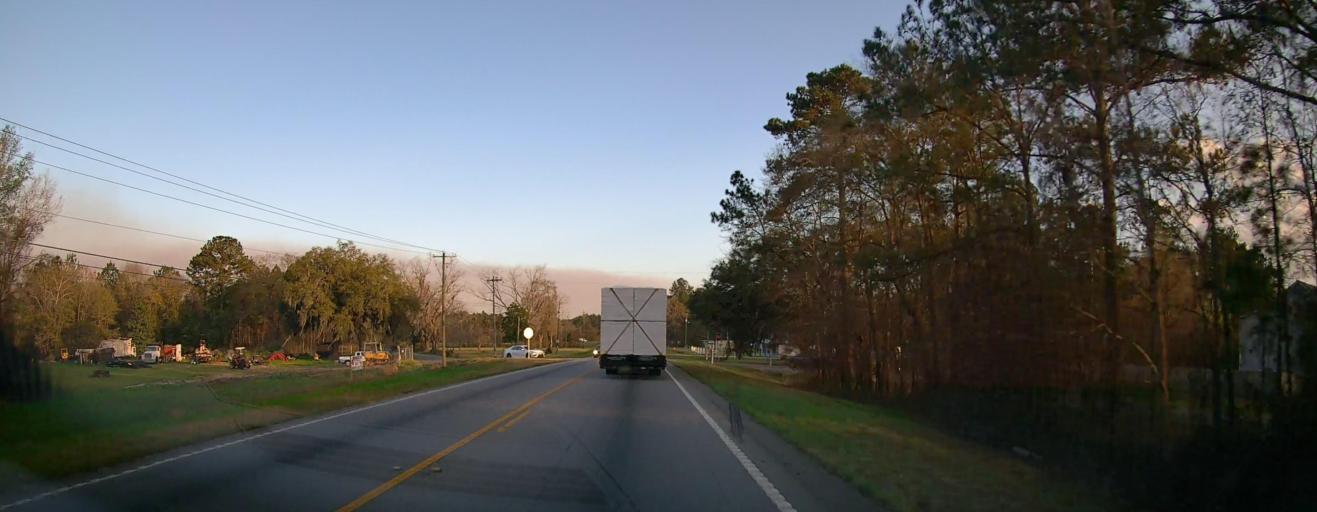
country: US
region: Georgia
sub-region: Chatham County
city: Bloomingdale
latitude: 32.1892
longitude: -81.4043
